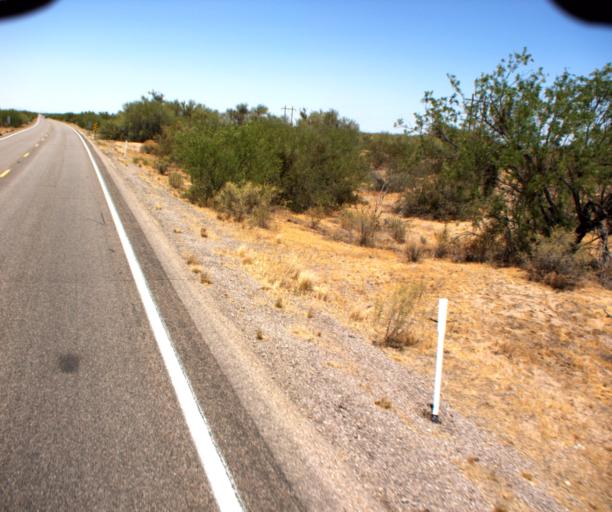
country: US
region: Arizona
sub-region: Pima County
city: Catalina
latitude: 32.7493
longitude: -111.1319
